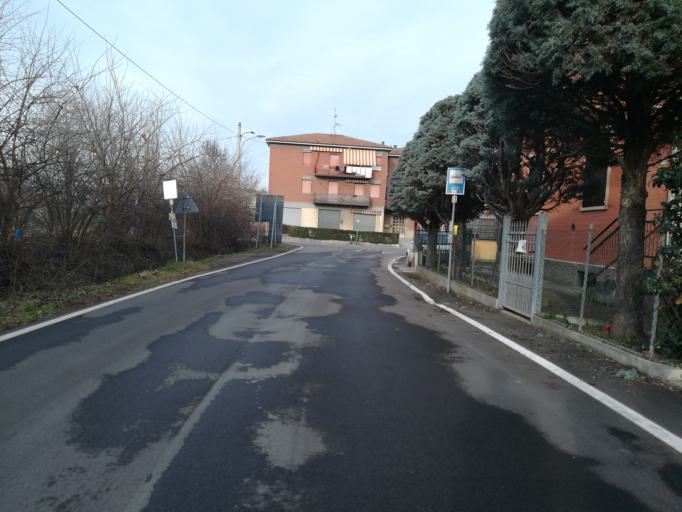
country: IT
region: Emilia-Romagna
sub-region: Provincia di Bologna
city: Progresso
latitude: 44.5508
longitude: 11.3526
